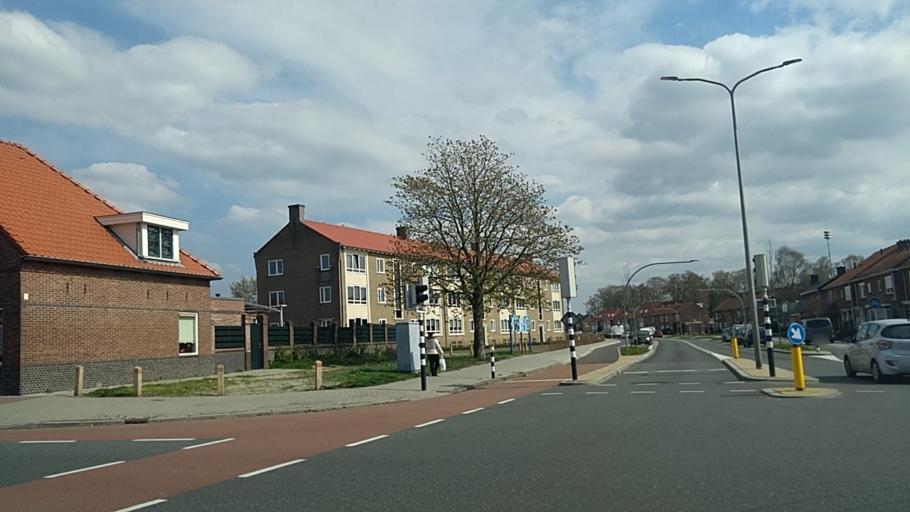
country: NL
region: Overijssel
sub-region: Gemeente Almelo
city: Almelo
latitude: 52.3475
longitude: 6.6501
